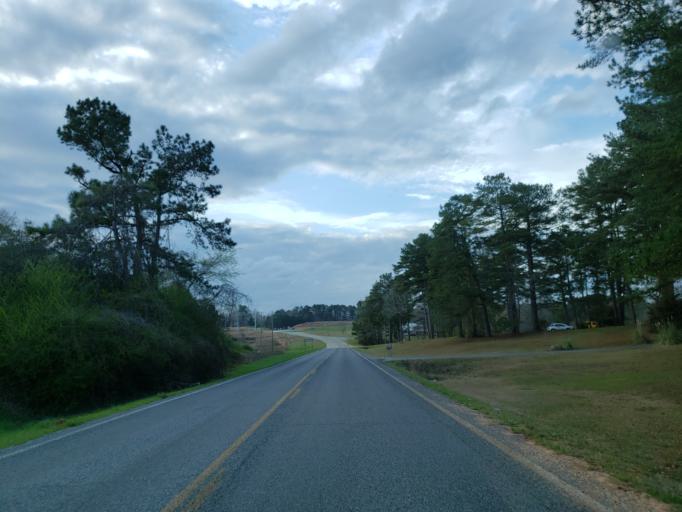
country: US
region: Mississippi
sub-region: Clarke County
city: Stonewall
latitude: 32.2095
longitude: -88.6941
